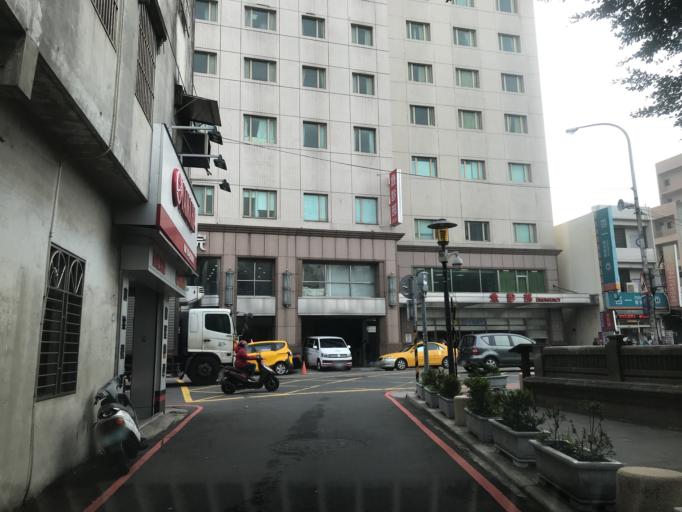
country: TW
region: Taiwan
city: Taoyuan City
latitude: 24.9632
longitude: 121.2288
